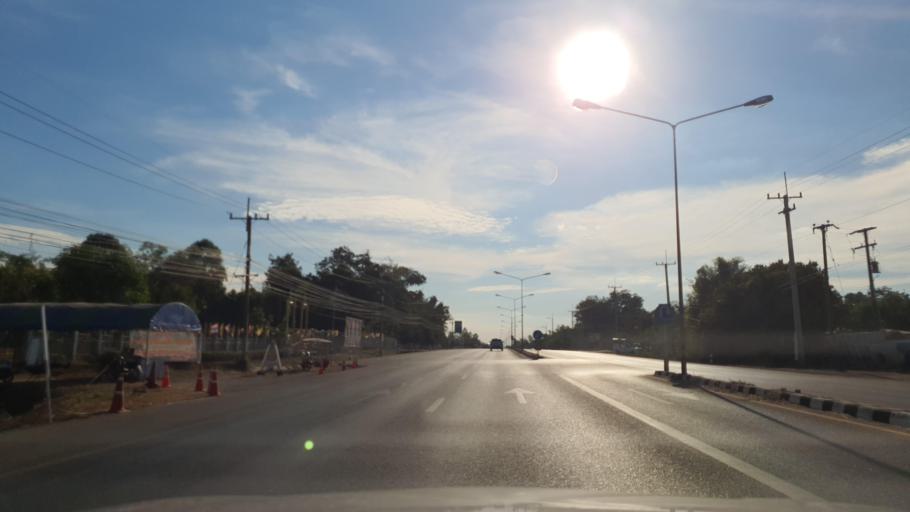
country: TH
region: Maha Sarakham
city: Kantharawichai
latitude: 16.3479
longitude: 103.3229
